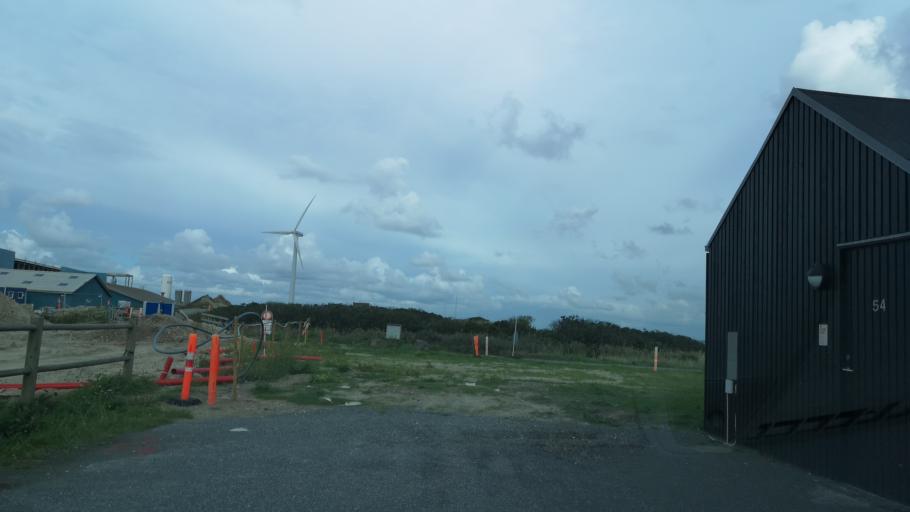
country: DK
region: Central Jutland
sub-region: Ringkobing-Skjern Kommune
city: Hvide Sande
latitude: 56.0063
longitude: 8.1354
